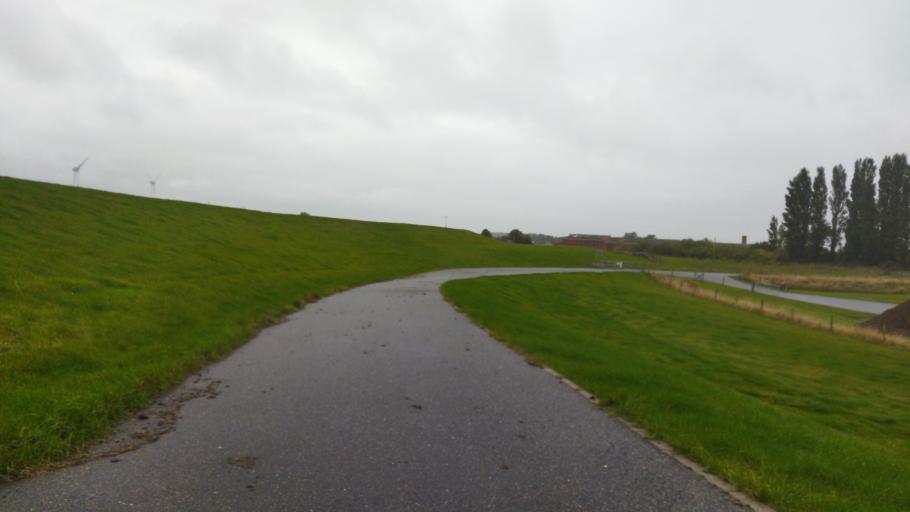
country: NL
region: Groningen
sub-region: Gemeente Delfzijl
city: Delfzijl
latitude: 53.3373
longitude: 7.0548
